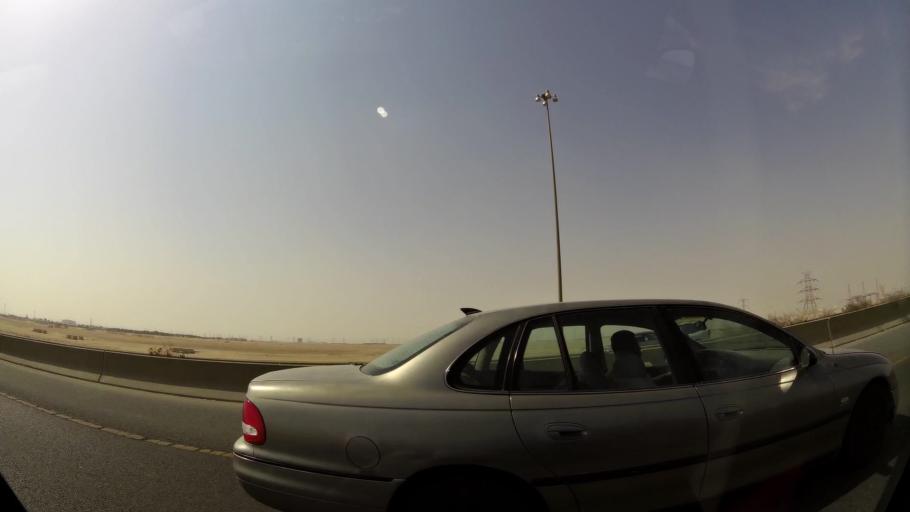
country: KW
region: Al Ahmadi
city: Al Fahahil
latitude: 29.0347
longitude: 48.1197
